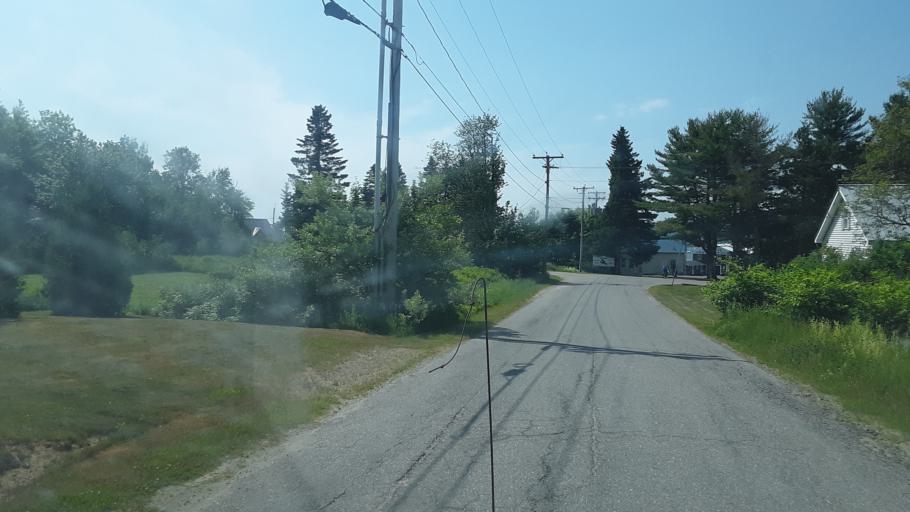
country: US
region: Maine
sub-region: Waldo County
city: Belfast
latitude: 44.4321
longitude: -68.9966
